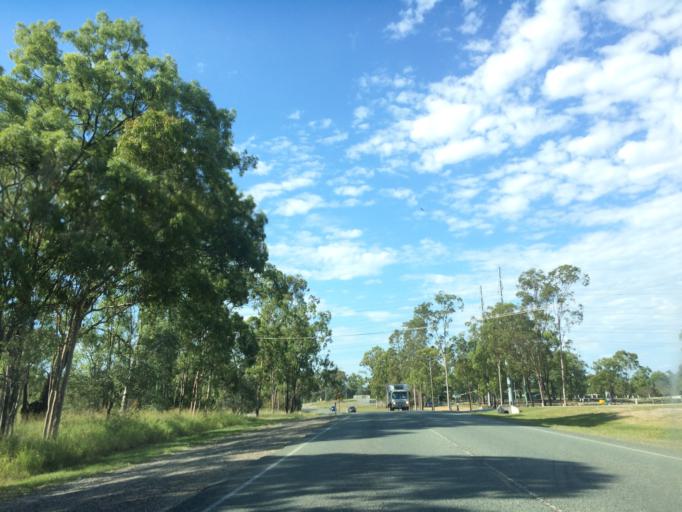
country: AU
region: Queensland
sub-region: Logan
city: Park Ridge South
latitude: -27.7273
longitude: 152.9843
